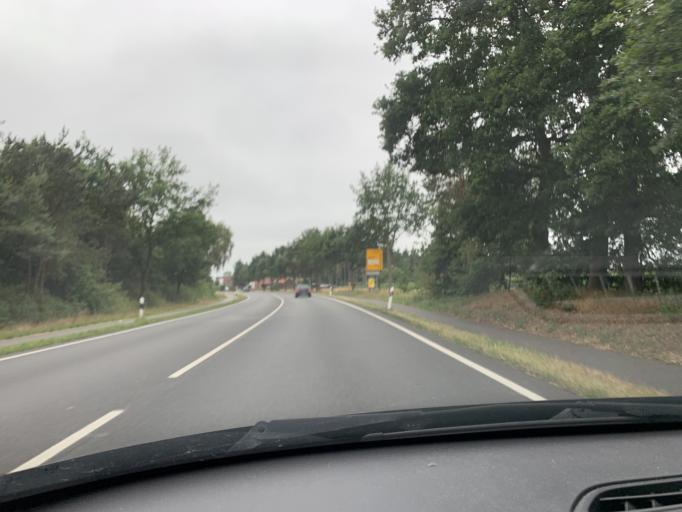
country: DE
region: Lower Saxony
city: Bawinkel
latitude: 52.6065
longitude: 7.4158
